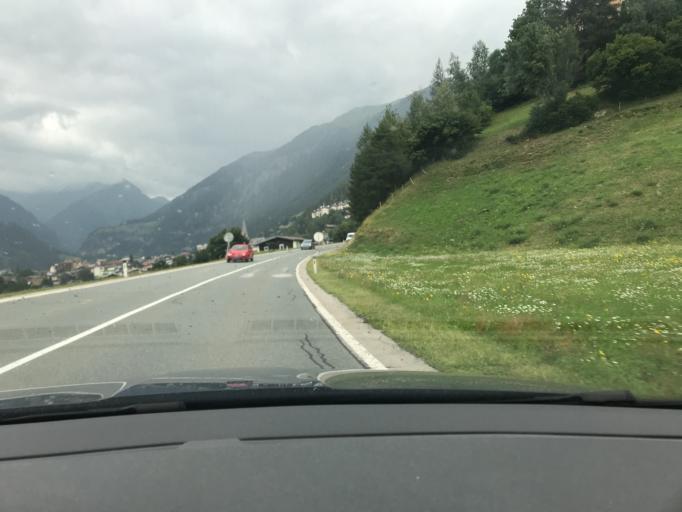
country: AT
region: Tyrol
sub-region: Politischer Bezirk Lienz
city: Matrei in Osttirol
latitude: 46.9923
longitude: 12.5432
